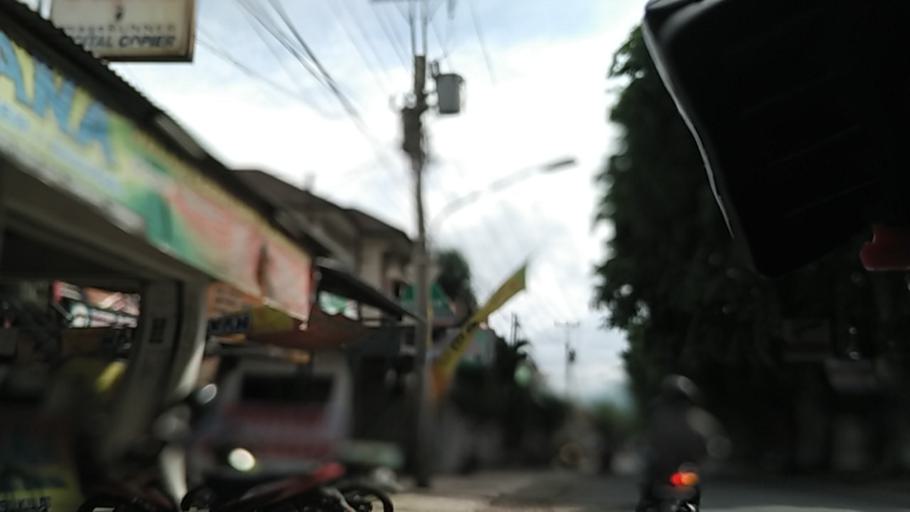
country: ID
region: Central Java
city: Semarang
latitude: -7.0558
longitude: 110.4362
